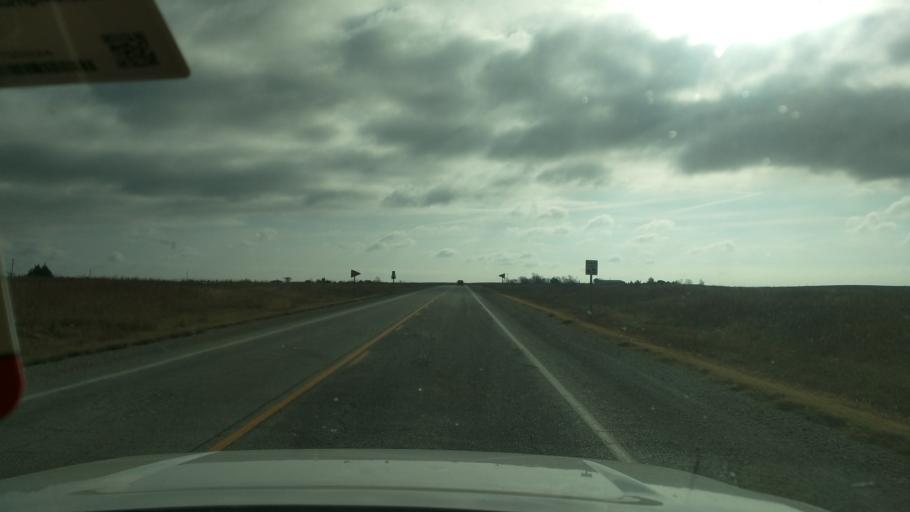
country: US
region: Kansas
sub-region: Chautauqua County
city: Sedan
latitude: 37.1058
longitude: -96.2456
